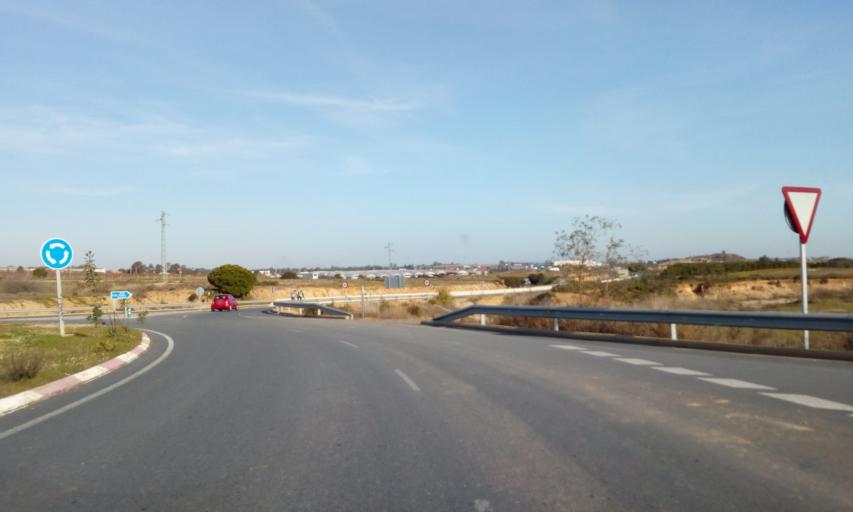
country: ES
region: Andalusia
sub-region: Provincia de Huelva
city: Lepe
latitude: 37.2379
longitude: -7.2351
